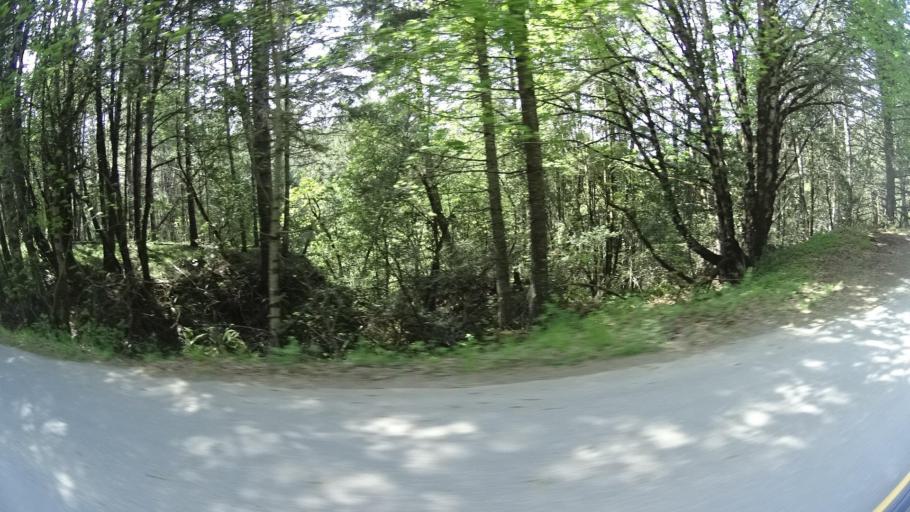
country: US
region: California
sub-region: Humboldt County
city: Redway
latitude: 40.4162
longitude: -123.7618
